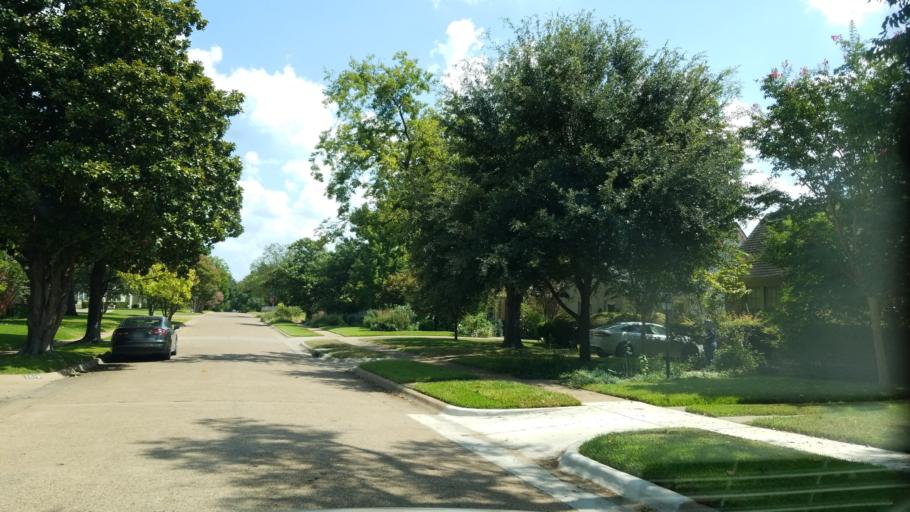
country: US
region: Texas
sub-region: Dallas County
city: Cockrell Hill
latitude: 32.7592
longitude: -96.8558
